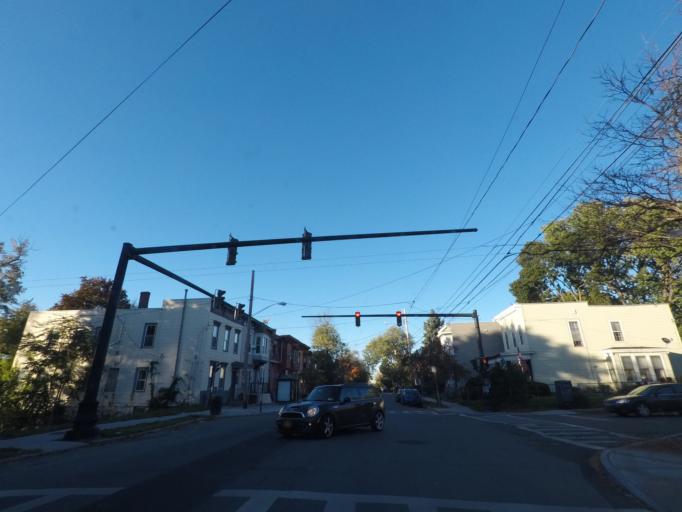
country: US
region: New York
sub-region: Albany County
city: Green Island
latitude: 42.7563
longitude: -73.6825
